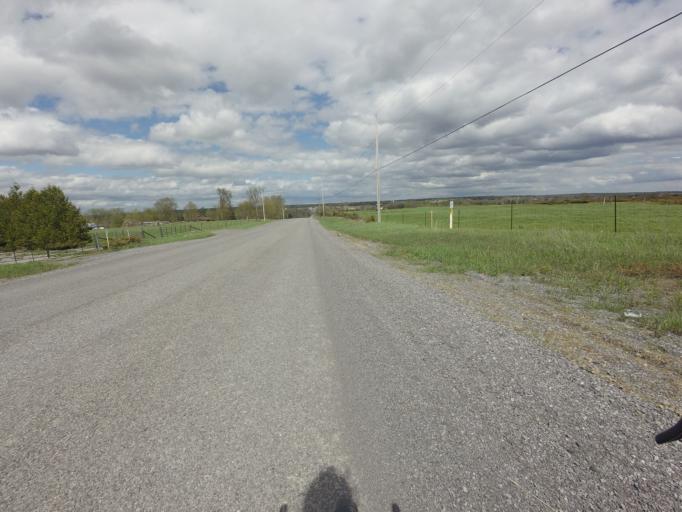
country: CA
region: Ontario
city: Carleton Place
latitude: 45.3043
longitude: -76.2086
